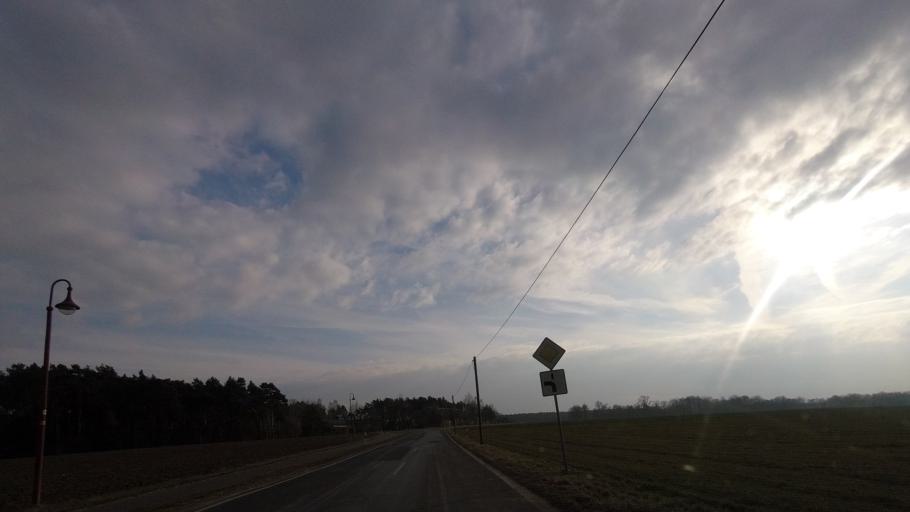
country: DE
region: Brandenburg
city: Belzig
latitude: 52.1677
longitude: 12.6798
